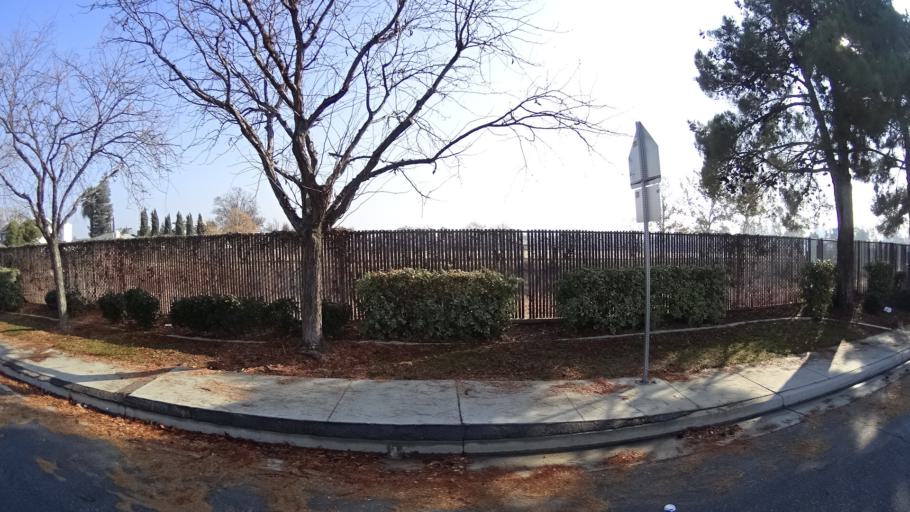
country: US
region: California
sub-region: Kern County
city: Greenacres
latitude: 35.3918
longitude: -119.1083
